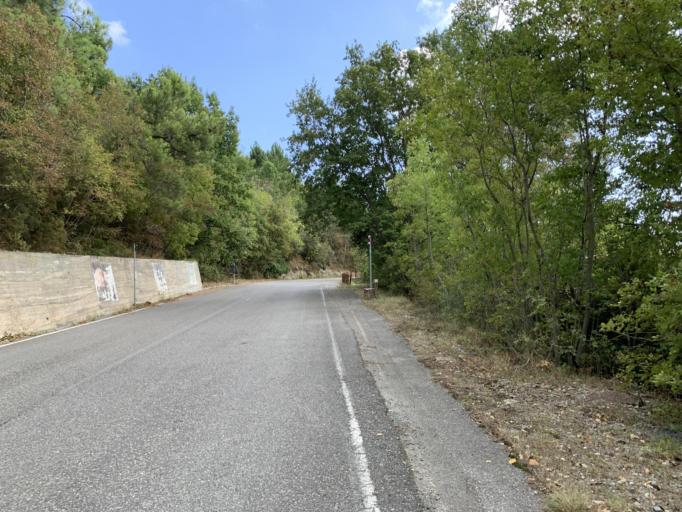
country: IT
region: Liguria
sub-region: Provincia di Savona
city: Feglino
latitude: 44.2206
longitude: 8.3078
